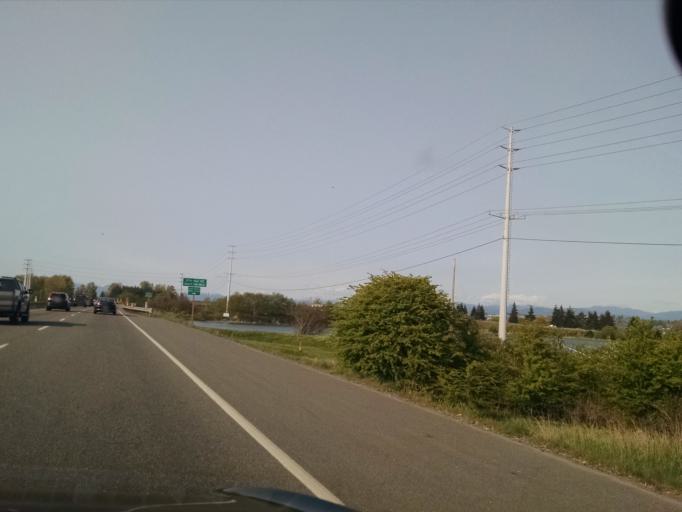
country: US
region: Washington
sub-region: Snohomish County
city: Marysville
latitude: 48.0296
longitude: -122.1832
